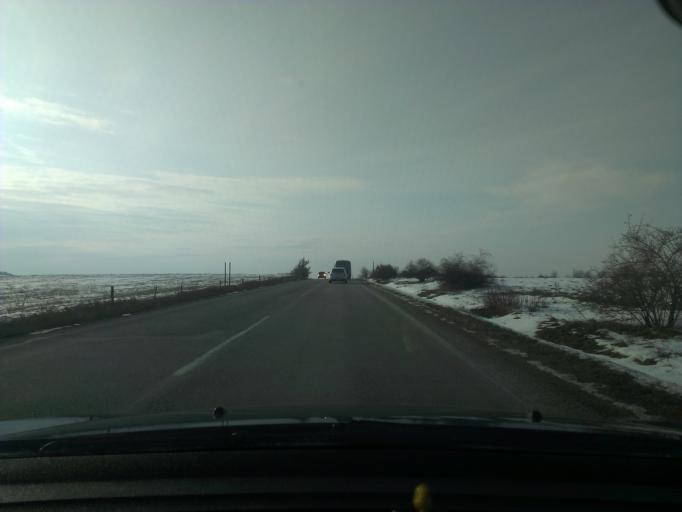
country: SK
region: Trenciansky
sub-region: Okres Myjava
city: Myjava
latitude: 48.7580
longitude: 17.6094
